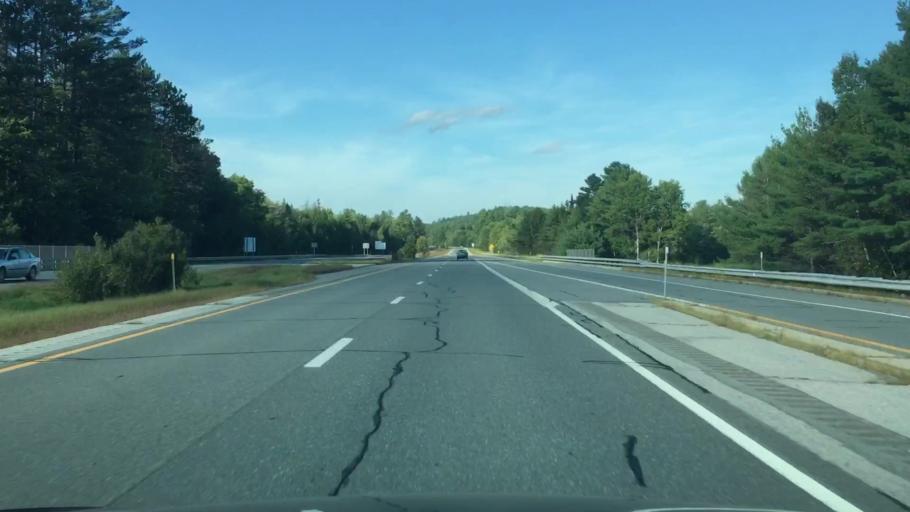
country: US
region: New Hampshire
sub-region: Grafton County
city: Littleton
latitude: 44.2598
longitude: -71.7523
